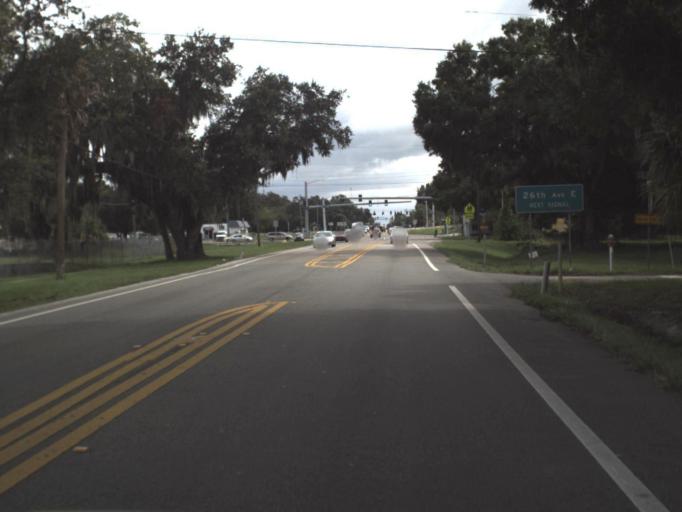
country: US
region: Florida
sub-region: Manatee County
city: Samoset
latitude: 27.4787
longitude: -82.5467
